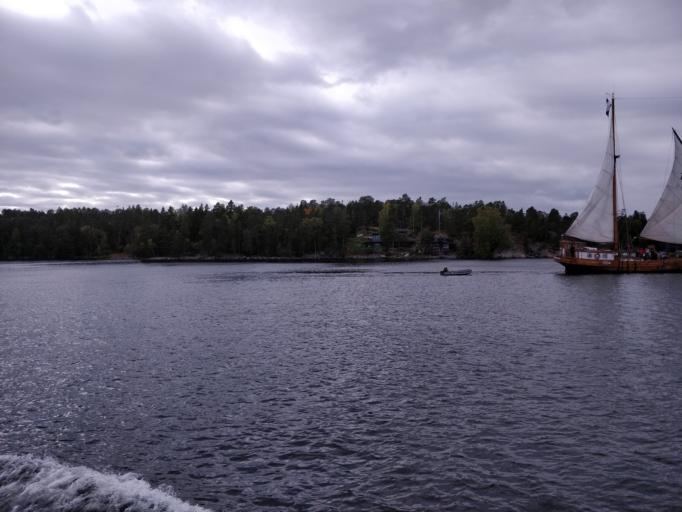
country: FI
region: Uusimaa
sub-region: Helsinki
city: Vantaa
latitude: 60.1697
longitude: 25.0960
